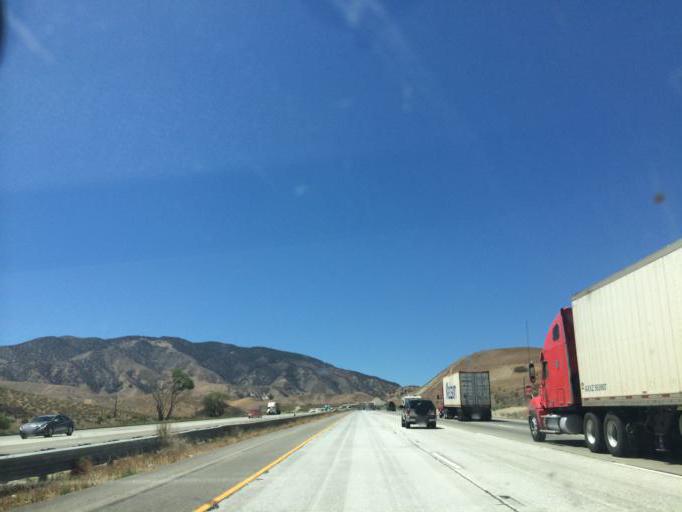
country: US
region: California
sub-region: Kern County
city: Lebec
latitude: 34.7963
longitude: -118.8610
